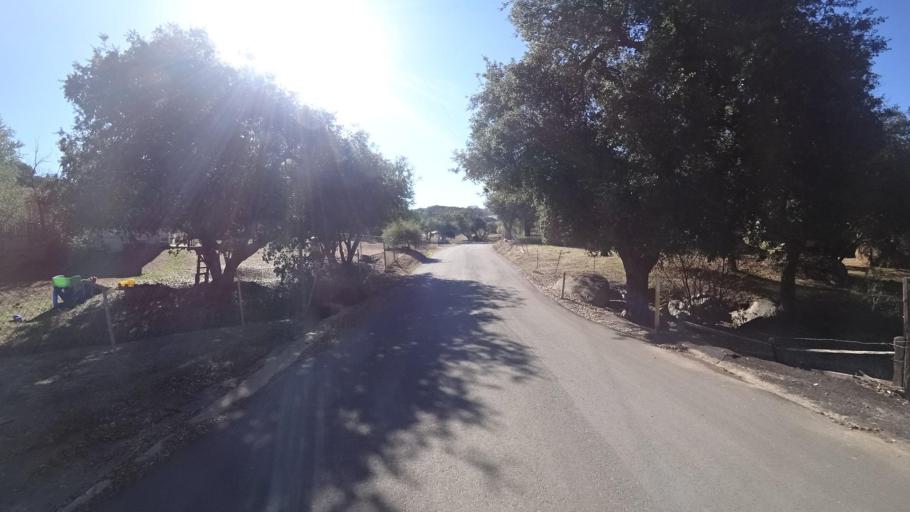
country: MX
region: Baja California
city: Tecate
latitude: 32.6768
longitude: -116.7289
